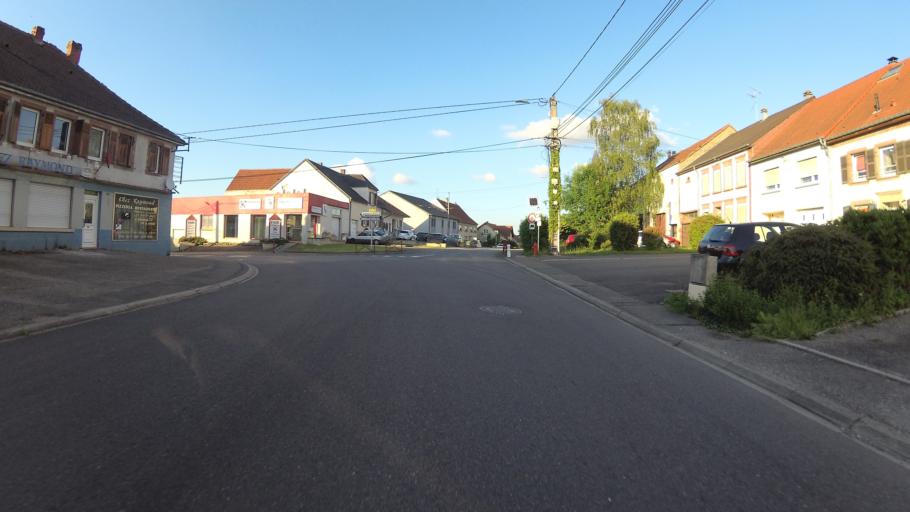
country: FR
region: Lorraine
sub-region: Departement de la Moselle
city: Remelfing
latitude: 49.0617
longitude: 7.0913
